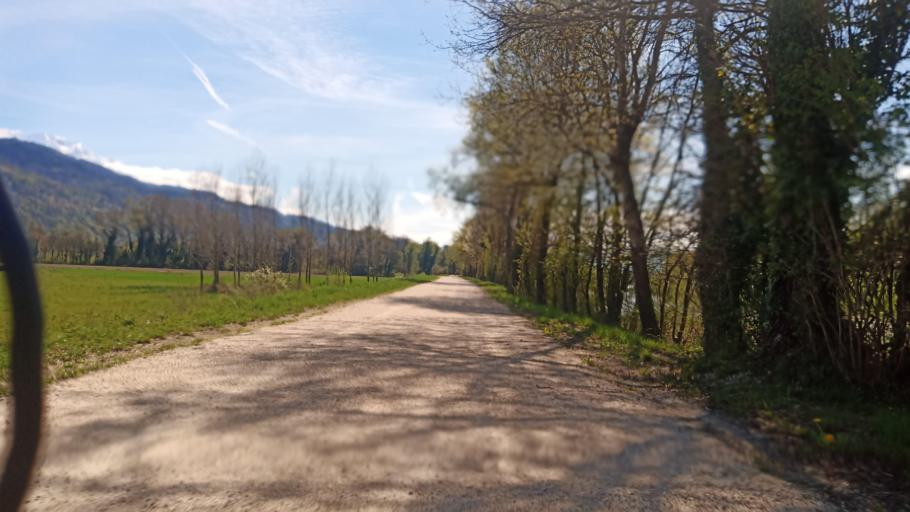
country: FR
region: Rhone-Alpes
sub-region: Departement de l'Isere
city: Tencin
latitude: 45.3260
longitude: 5.9590
